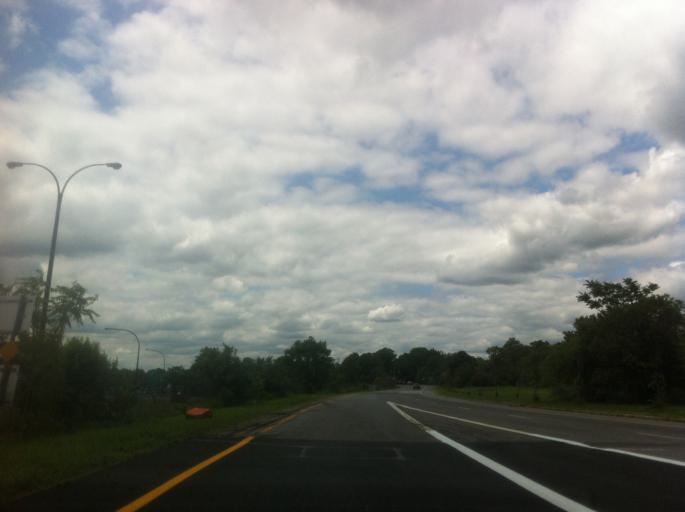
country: US
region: New York
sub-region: Nassau County
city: Jericho
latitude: 40.7865
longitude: -73.5296
